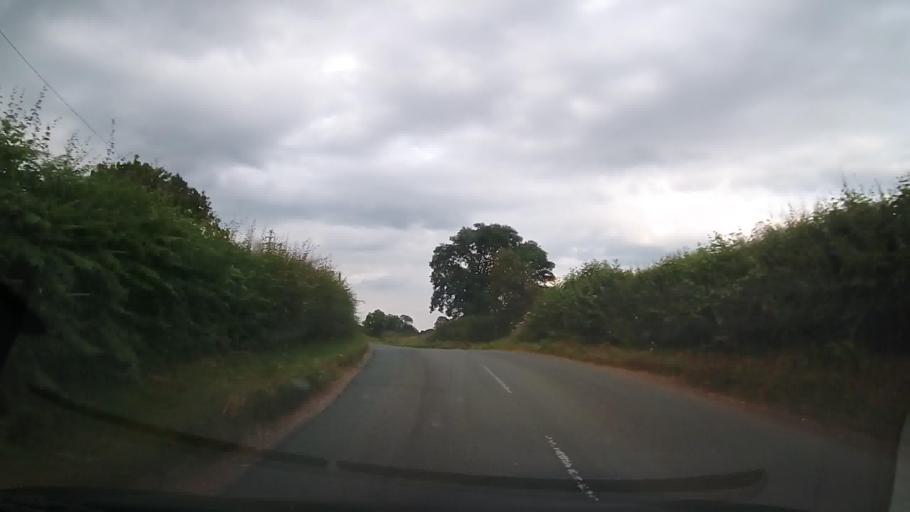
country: GB
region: Wales
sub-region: Sir Powys
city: Llanrhaeadr-ym-Mochnant
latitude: 52.8100
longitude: -3.3253
